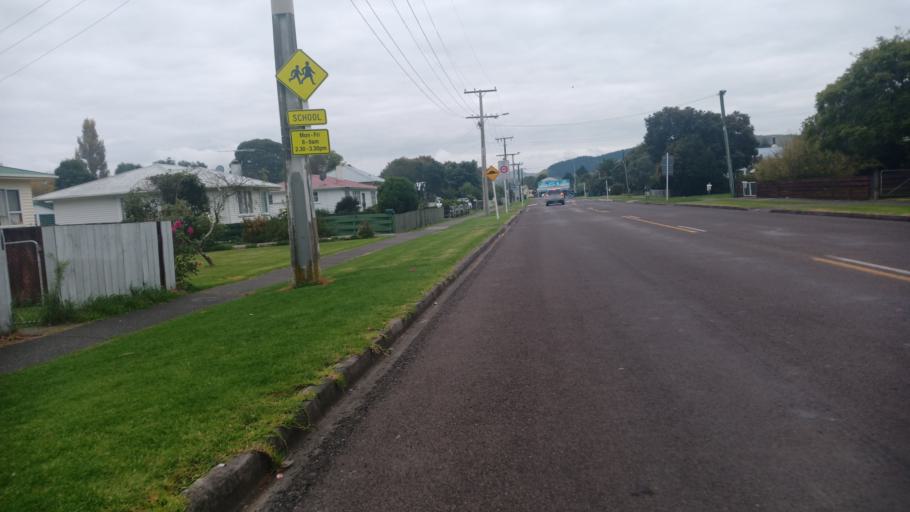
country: NZ
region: Gisborne
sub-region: Gisborne District
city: Gisborne
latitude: -38.6766
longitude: 178.0423
